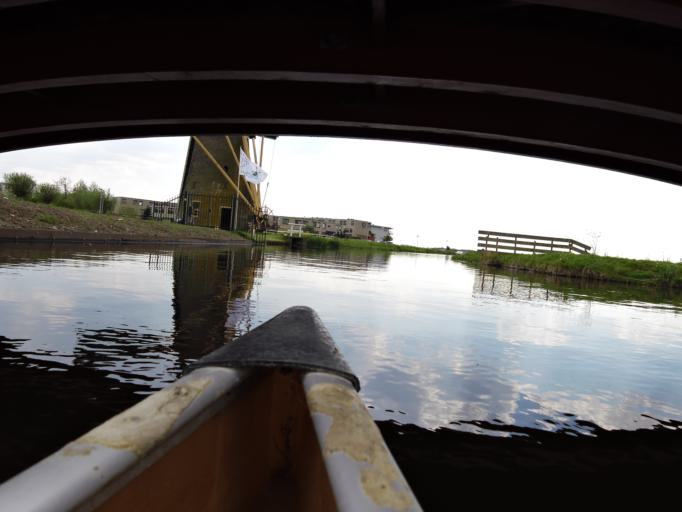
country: NL
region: South Holland
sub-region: Gemeente Voorschoten
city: Voorschoten
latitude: 52.1511
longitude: 4.4432
